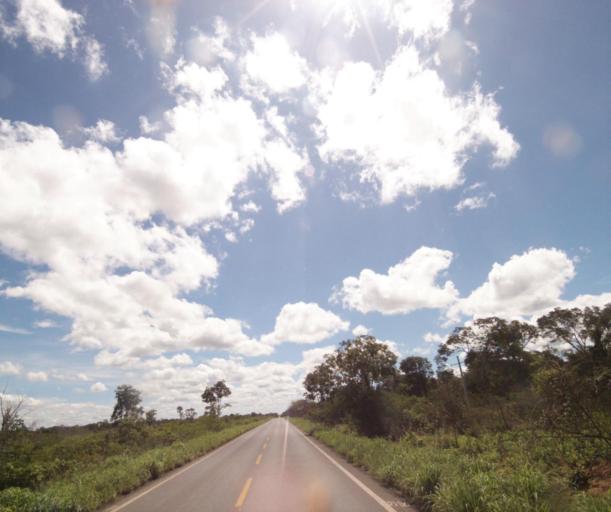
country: BR
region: Bahia
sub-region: Sao Felix Do Coribe
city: Santa Maria da Vitoria
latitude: -13.3941
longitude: -44.1294
